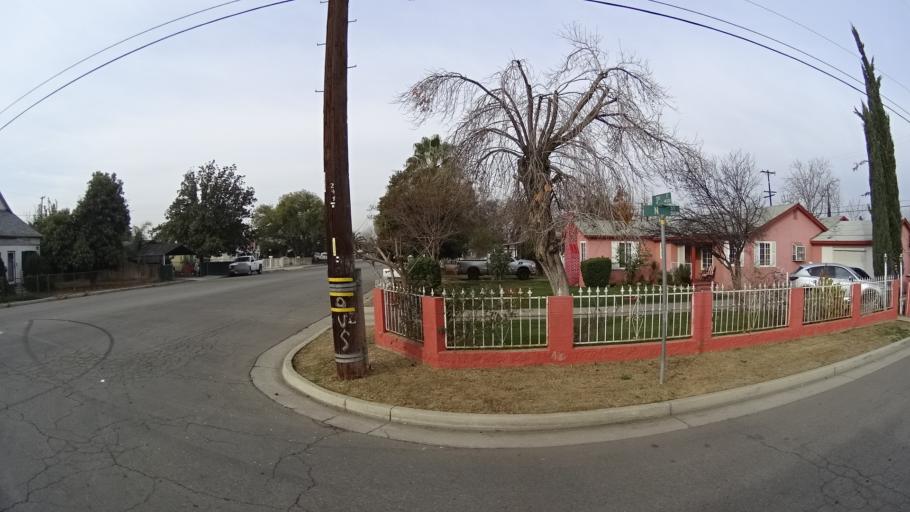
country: US
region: California
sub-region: Kern County
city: Bakersfield
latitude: 35.3590
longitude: -119.0142
